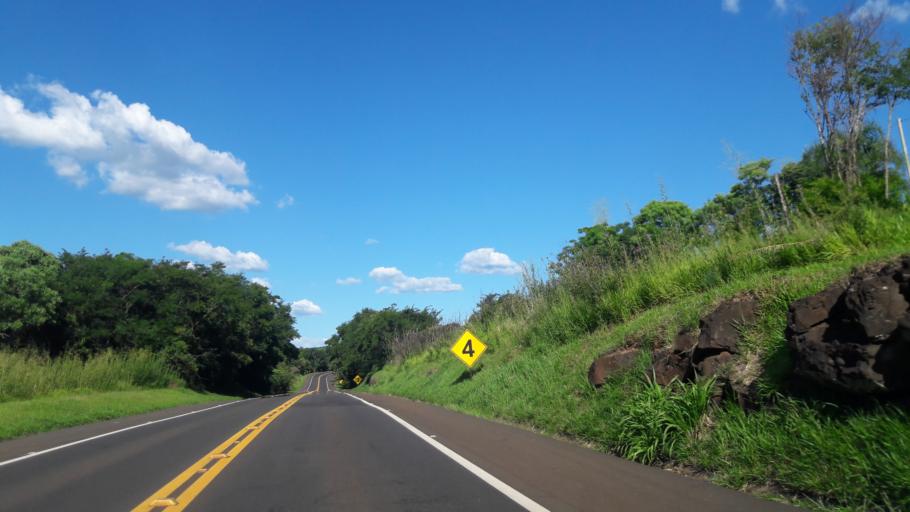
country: BR
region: Parana
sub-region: Laranjeiras Do Sul
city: Laranjeiras do Sul
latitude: -25.4205
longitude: -52.0386
